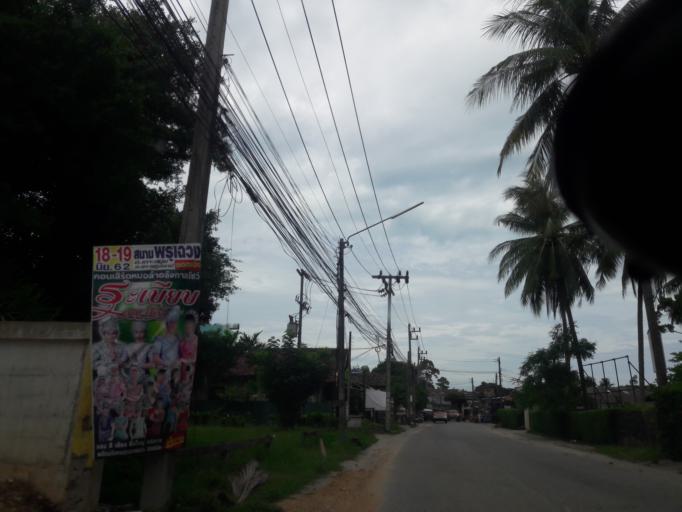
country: TH
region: Surat Thani
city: Ko Samui
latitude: 9.5352
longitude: 100.0435
